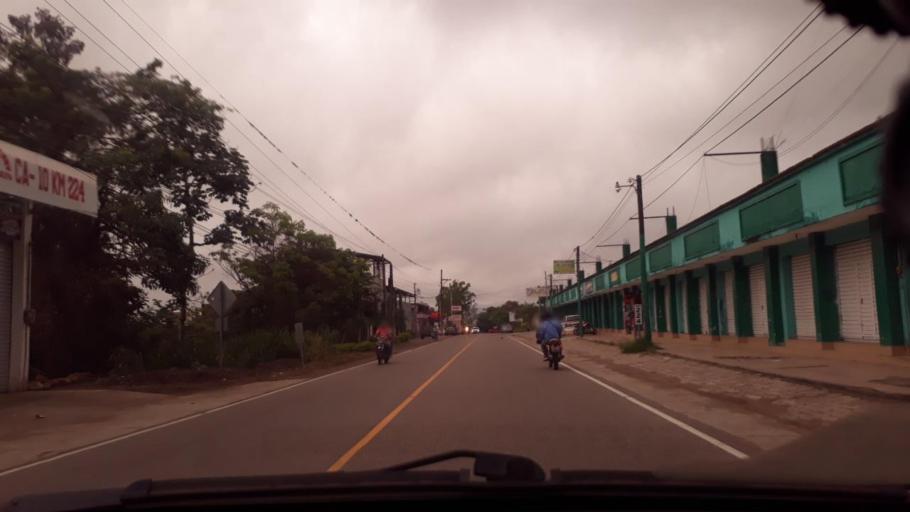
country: GT
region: Chiquimula
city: Esquipulas
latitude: 14.5596
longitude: -89.3393
